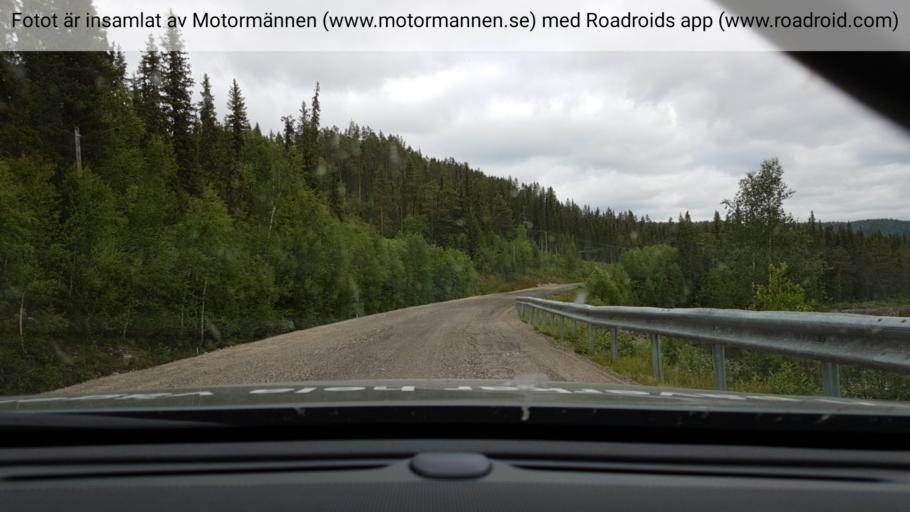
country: SE
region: Vaesterbotten
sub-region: Storumans Kommun
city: Fristad
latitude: 65.8178
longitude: 16.7924
